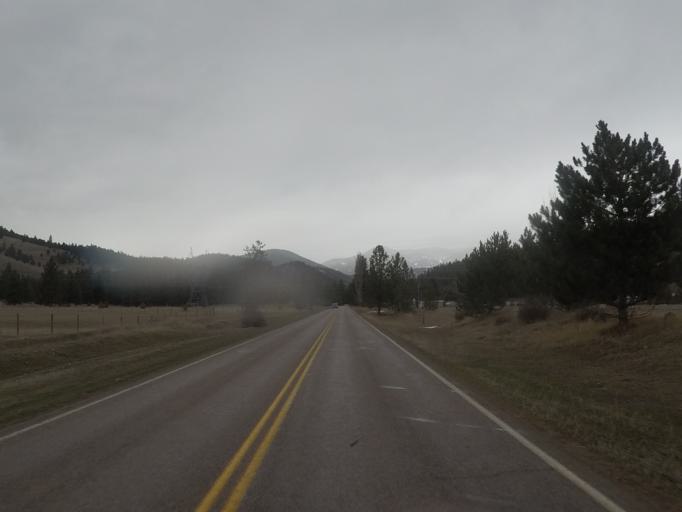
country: US
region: Montana
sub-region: Missoula County
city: East Missoula
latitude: 46.9046
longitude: -113.9604
